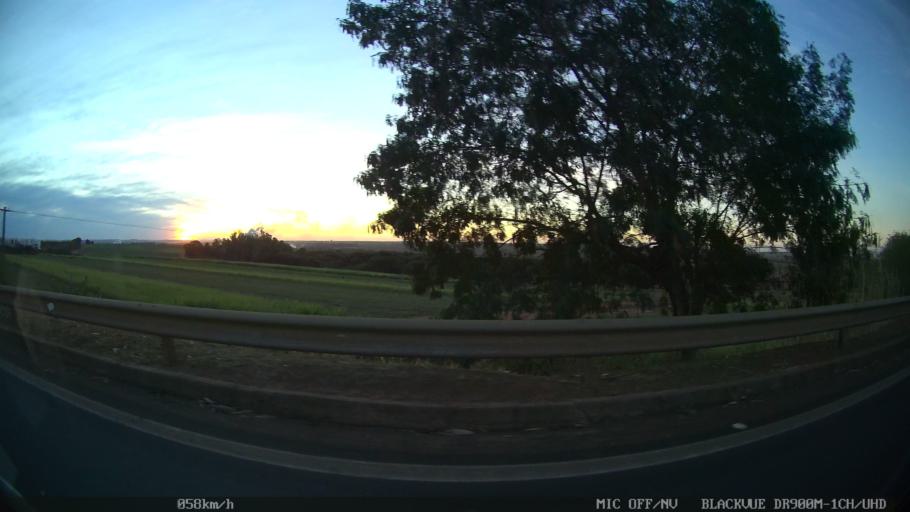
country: BR
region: Sao Paulo
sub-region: Catanduva
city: Catanduva
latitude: -21.1085
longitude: -48.9626
